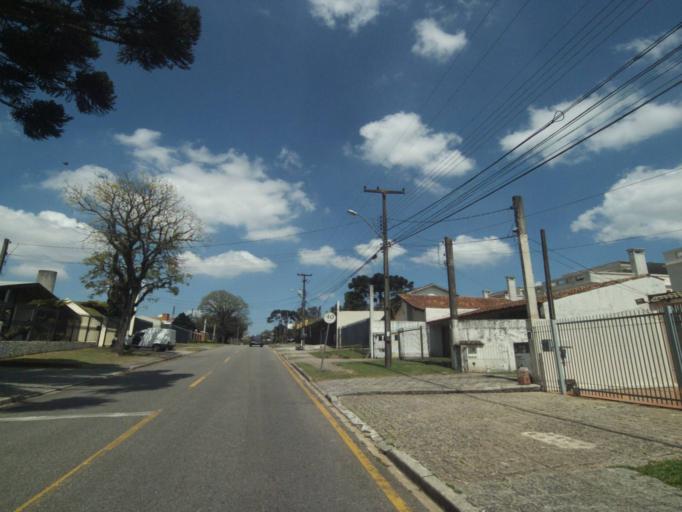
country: BR
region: Parana
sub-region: Curitiba
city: Curitiba
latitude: -25.4127
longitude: -49.2393
